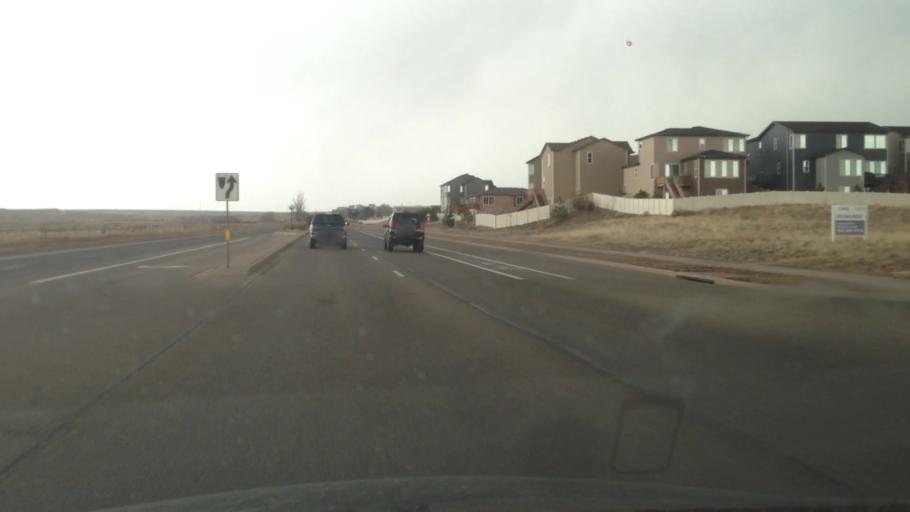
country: US
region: Colorado
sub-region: Douglas County
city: Parker
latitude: 39.4931
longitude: -104.7791
